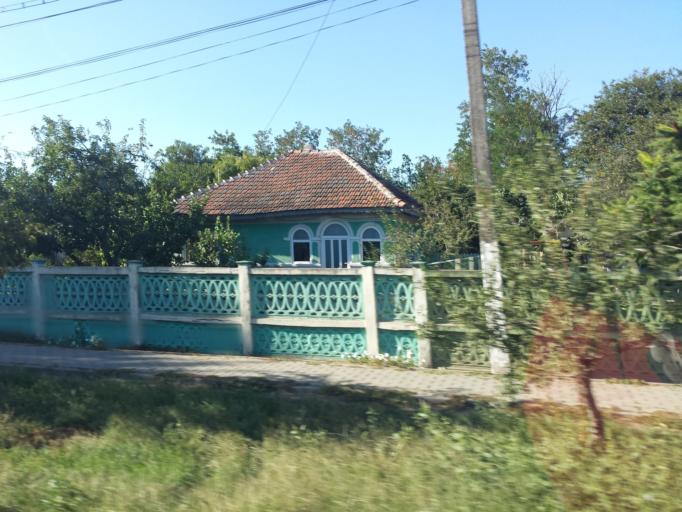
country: RO
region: Ialomita
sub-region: Comuna Ograda
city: Ograda
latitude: 44.6108
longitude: 27.5466
